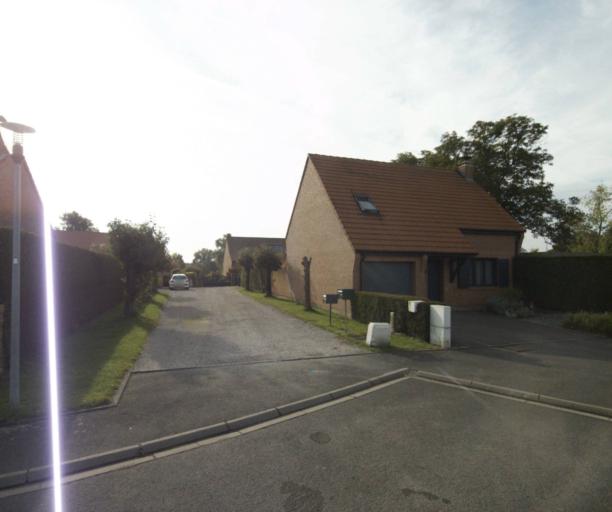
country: FR
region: Nord-Pas-de-Calais
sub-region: Departement du Nord
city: Sainghin-en-Weppes
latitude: 50.5565
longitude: 2.9007
